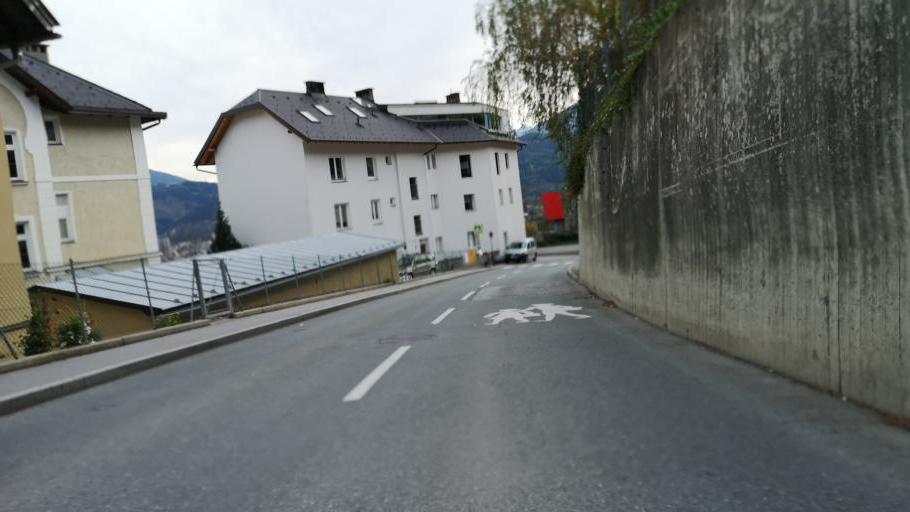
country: AT
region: Tyrol
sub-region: Innsbruck Stadt
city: Innsbruck
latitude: 47.2742
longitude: 11.3894
